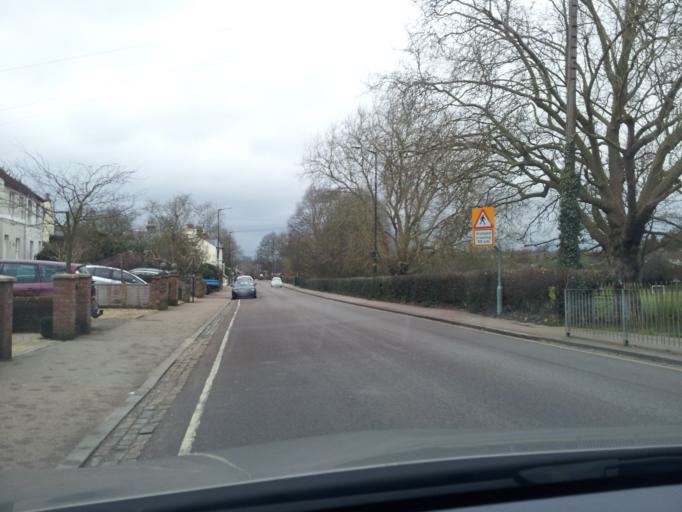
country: GB
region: England
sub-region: Hertfordshire
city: St Albans
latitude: 51.7549
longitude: -0.3449
